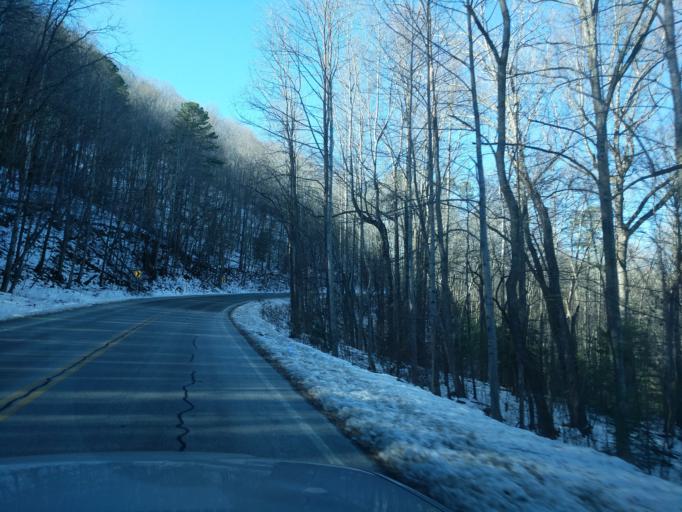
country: US
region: Georgia
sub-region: Rabun County
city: Clayton
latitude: 34.8890
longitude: -83.5789
